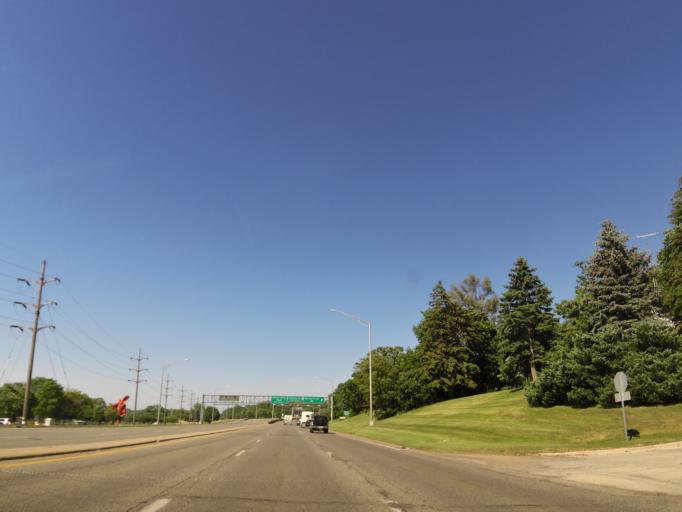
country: US
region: Illinois
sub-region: Winnebago County
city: Rockford
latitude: 42.2851
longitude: -89.0653
